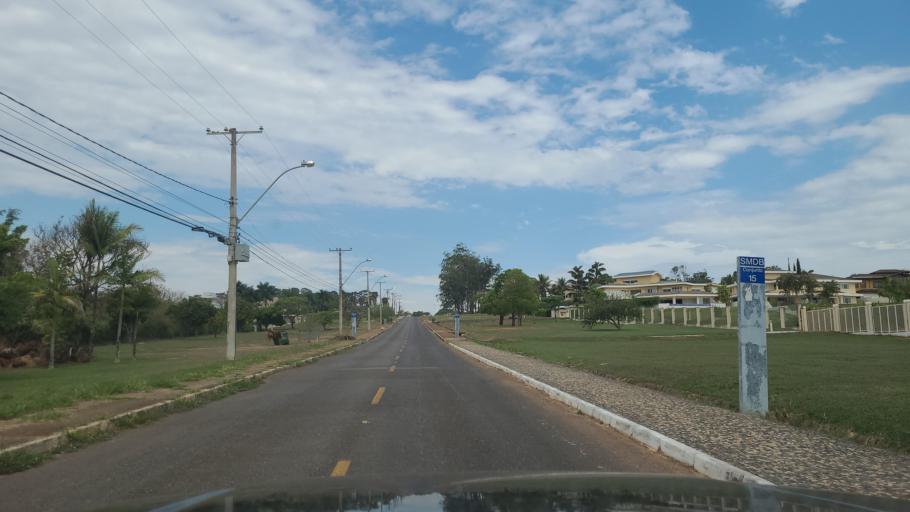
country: BR
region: Federal District
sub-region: Brasilia
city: Brasilia
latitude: -15.8572
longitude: -47.8461
